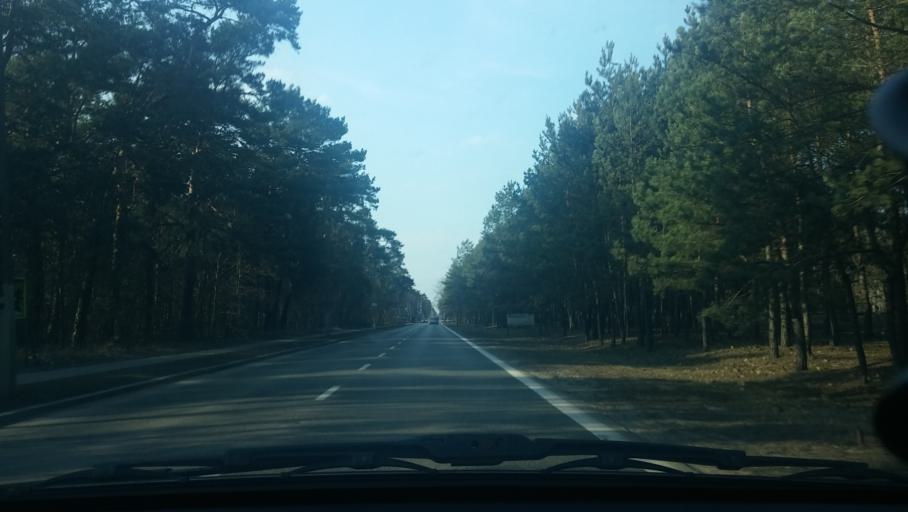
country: PL
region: Masovian Voivodeship
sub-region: Warszawa
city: Wawer
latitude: 52.1759
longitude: 21.1966
